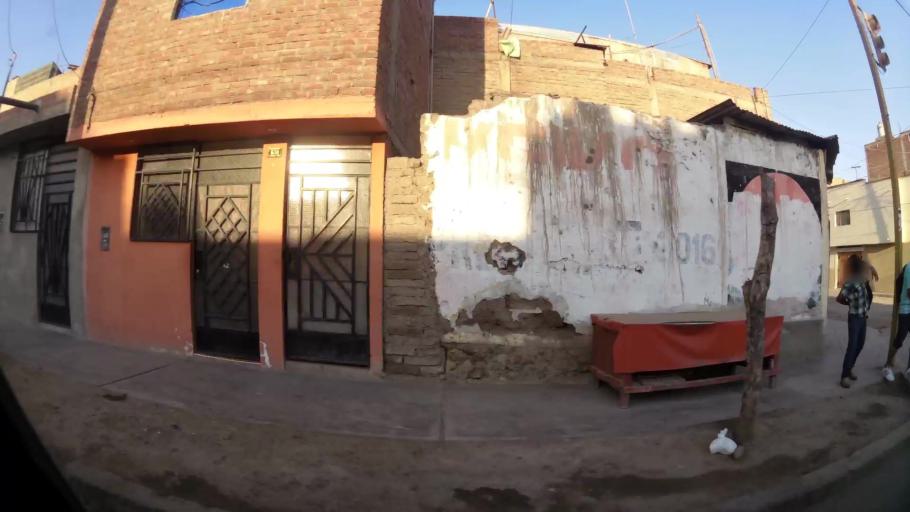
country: PE
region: Lambayeque
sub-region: Provincia de Chiclayo
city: Santa Rosa
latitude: -6.7697
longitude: -79.8297
